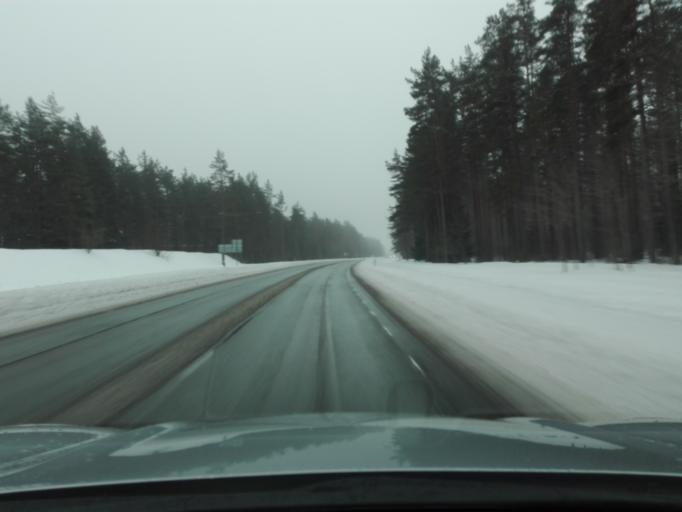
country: EE
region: Harju
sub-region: Kiili vald
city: Kiili
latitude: 59.3513
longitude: 24.7740
